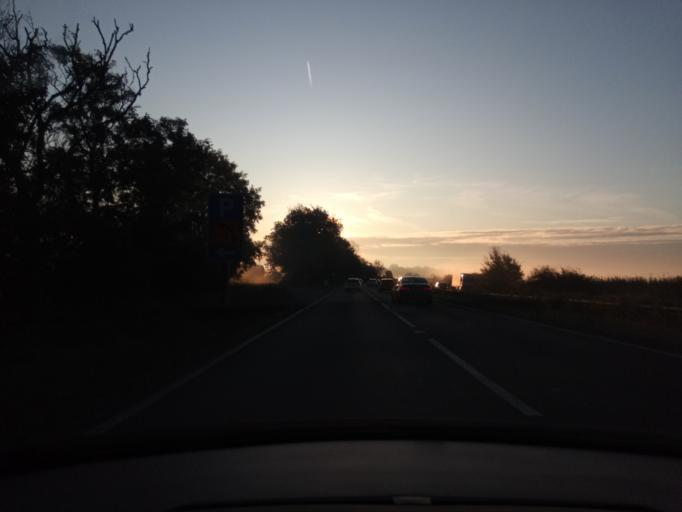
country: GB
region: England
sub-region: Peterborough
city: Castor
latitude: 52.5555
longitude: -0.3455
